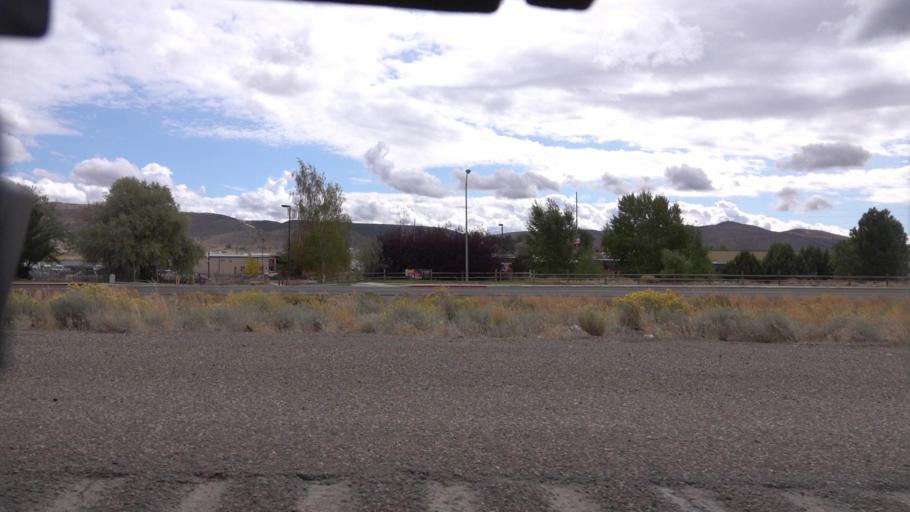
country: US
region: Nevada
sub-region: Elko County
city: Elko
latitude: 40.8629
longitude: -115.7354
